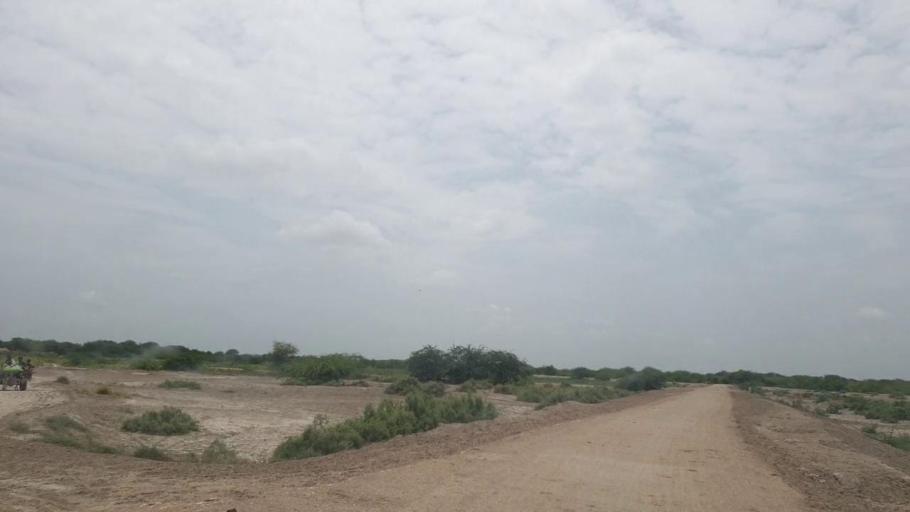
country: PK
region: Sindh
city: Naukot
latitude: 24.9333
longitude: 69.1826
